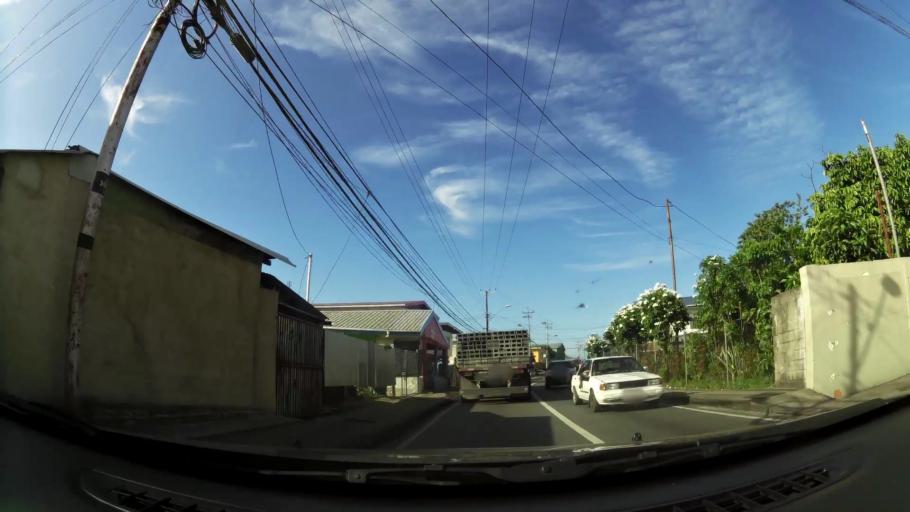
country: TT
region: Chaguanas
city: Chaguanas
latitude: 10.5278
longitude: -61.3832
